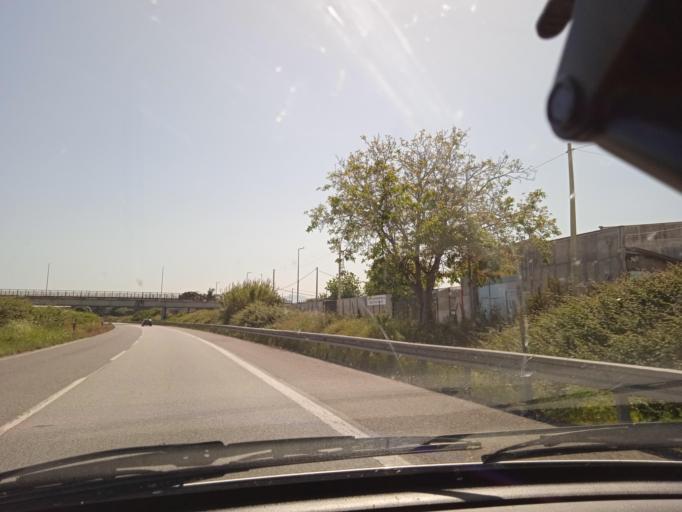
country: IT
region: Sicily
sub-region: Messina
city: Barcellona Pozzo di Gotto
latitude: 38.1642
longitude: 15.2082
